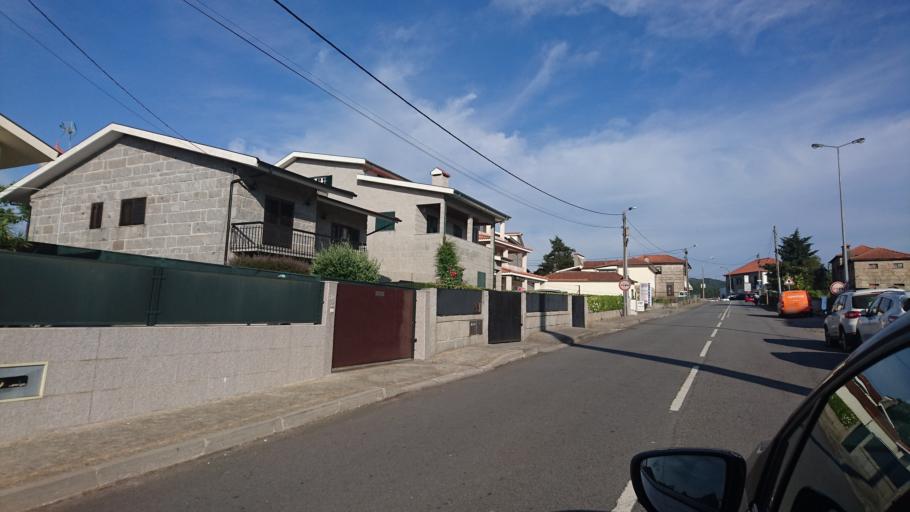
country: PT
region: Porto
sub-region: Paredes
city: Recarei
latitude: 41.1257
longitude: -8.3711
